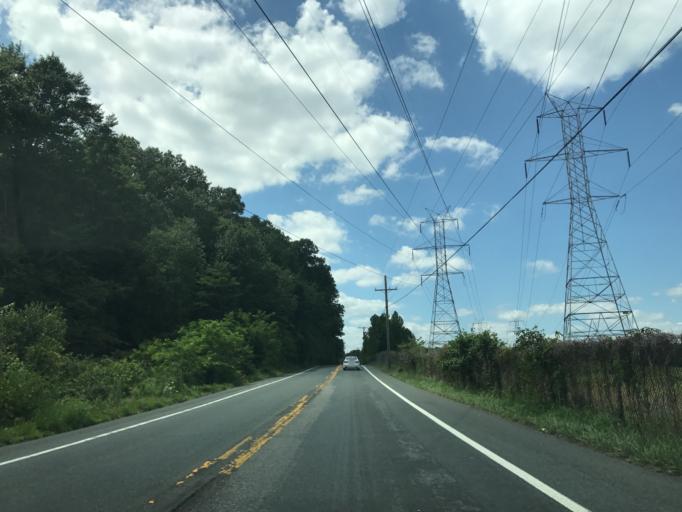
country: US
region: Maryland
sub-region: Anne Arundel County
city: Maryland City
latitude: 39.0450
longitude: -76.8018
